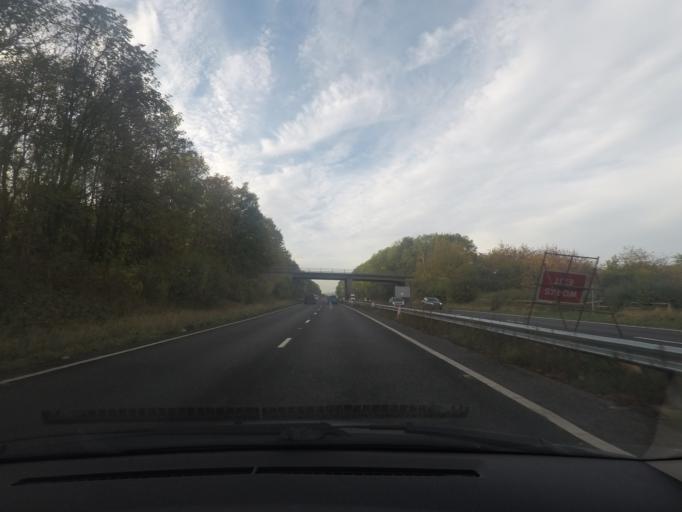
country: GB
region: England
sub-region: North Yorkshire
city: Tadcaster
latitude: 53.8856
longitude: -1.2494
